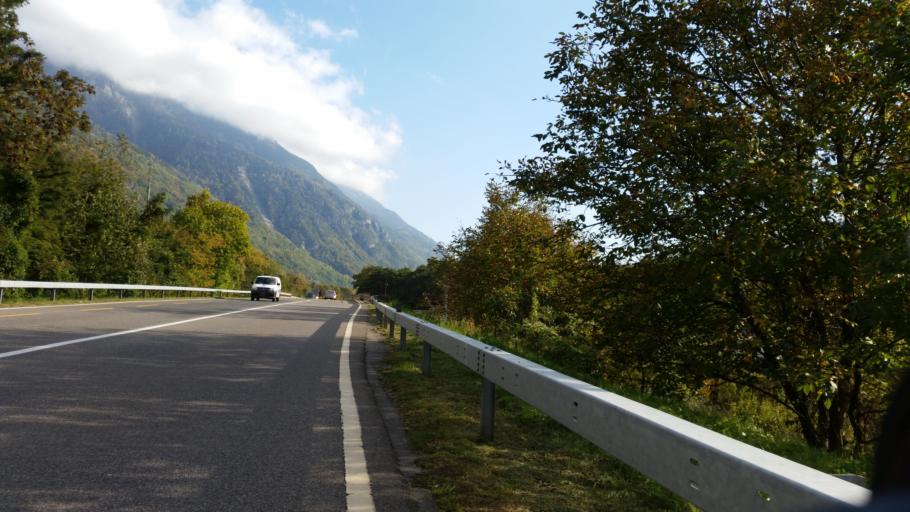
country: CH
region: Valais
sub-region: Martigny District
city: Evionnaz
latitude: 46.2003
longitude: 7.0172
